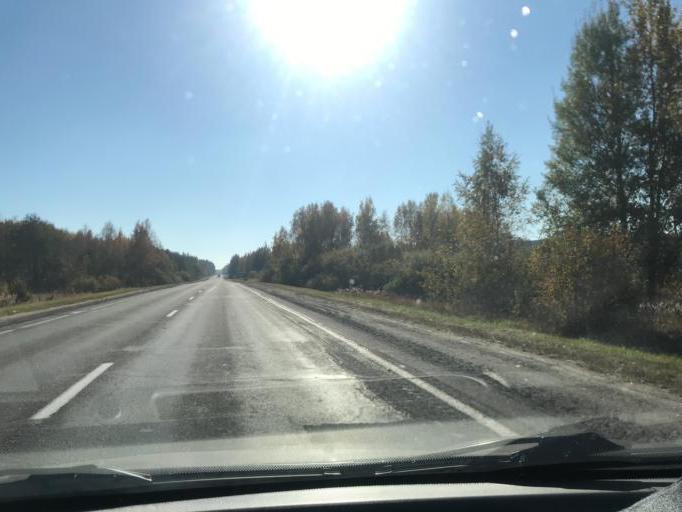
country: BY
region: Gomel
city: Kastsyukowka
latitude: 52.4412
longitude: 30.8255
